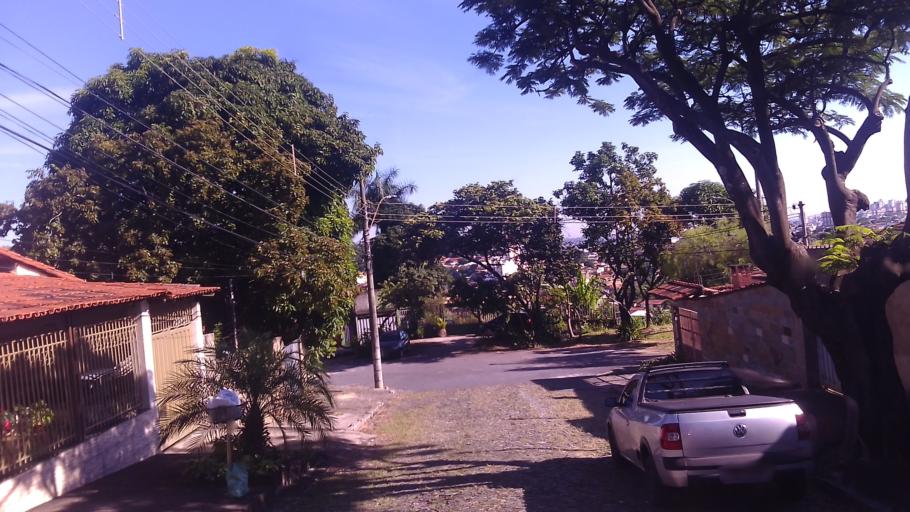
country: BR
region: Minas Gerais
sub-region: Contagem
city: Contagem
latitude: -19.9207
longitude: -44.0037
